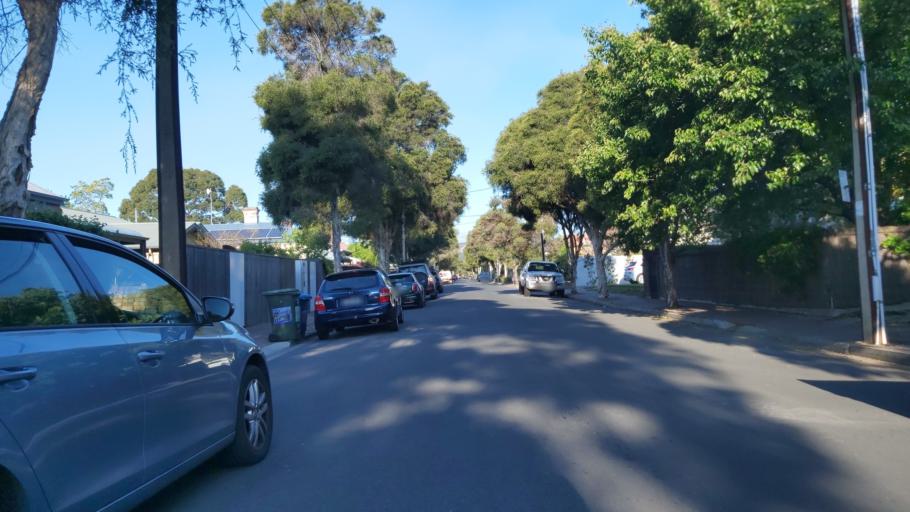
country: AU
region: South Australia
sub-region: Unley
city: Fullarton
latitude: -34.9462
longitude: 138.6150
